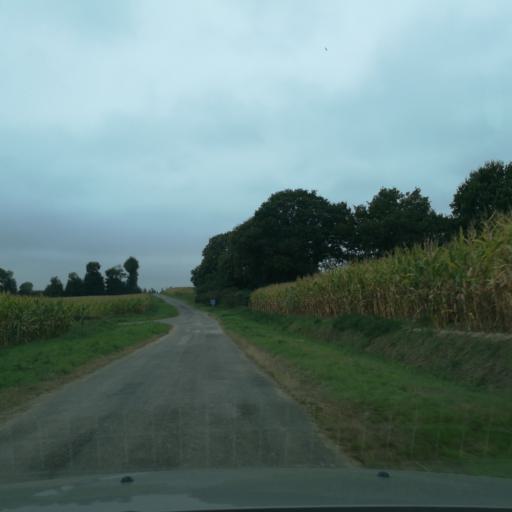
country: FR
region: Brittany
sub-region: Departement d'Ille-et-Vilaine
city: Montauban-de-Bretagne
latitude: 48.1875
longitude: -2.0256
